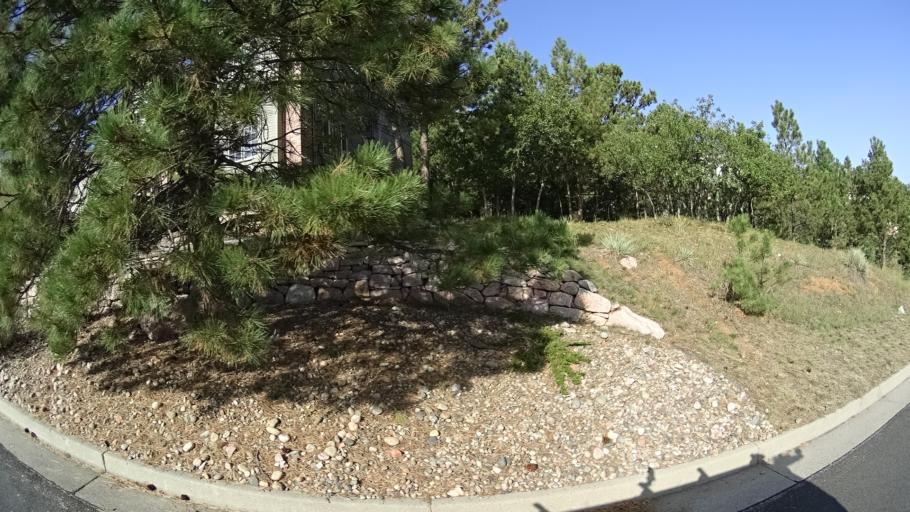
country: US
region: Colorado
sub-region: El Paso County
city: Colorado Springs
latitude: 38.8150
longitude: -104.8709
